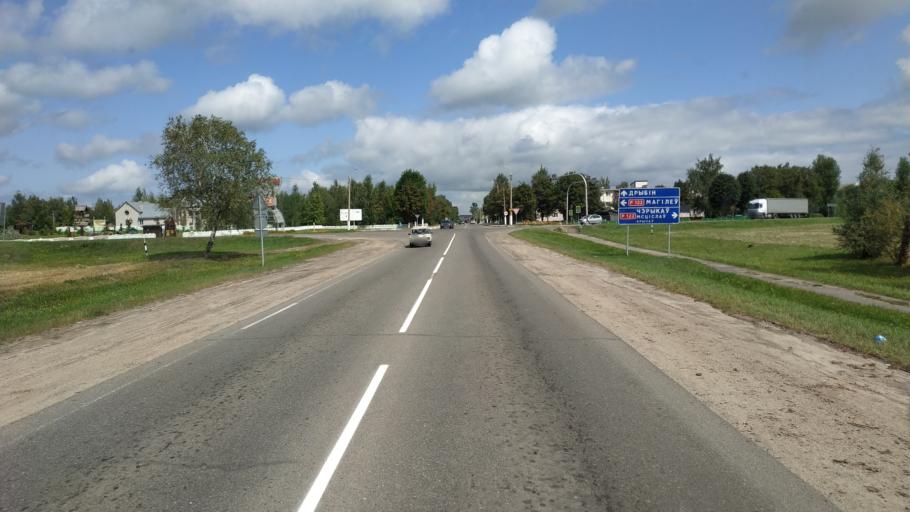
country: BY
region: Mogilev
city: Chavusy
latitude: 53.8010
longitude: 30.9527
